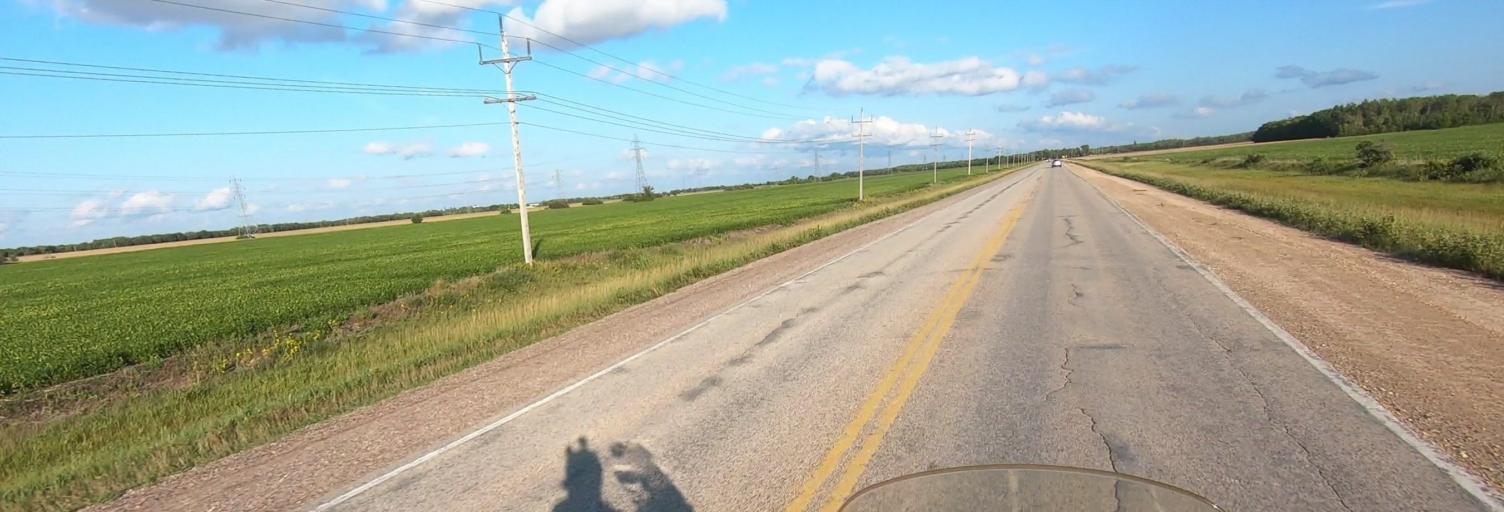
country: CA
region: Manitoba
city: Selkirk
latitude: 50.1202
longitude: -96.8548
